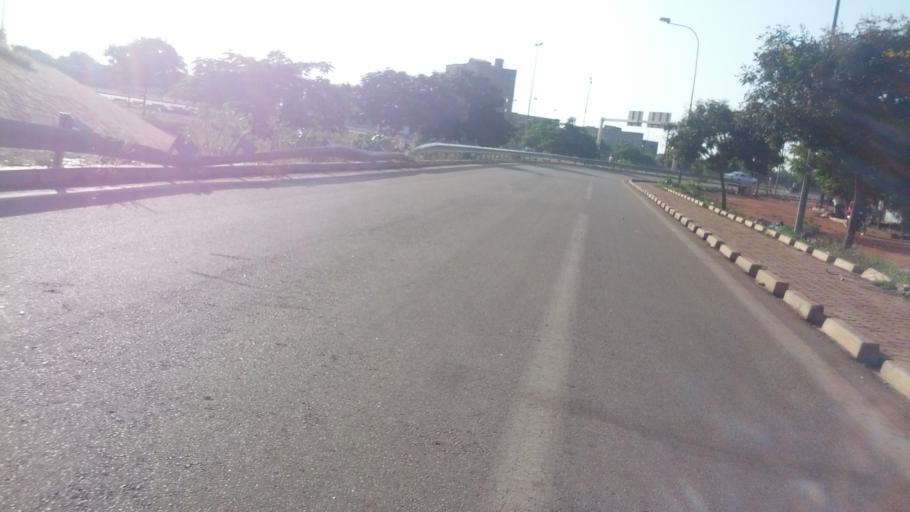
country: BF
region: Centre
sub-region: Kadiogo Province
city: Ouagadougou
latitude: 12.3312
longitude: -1.5035
